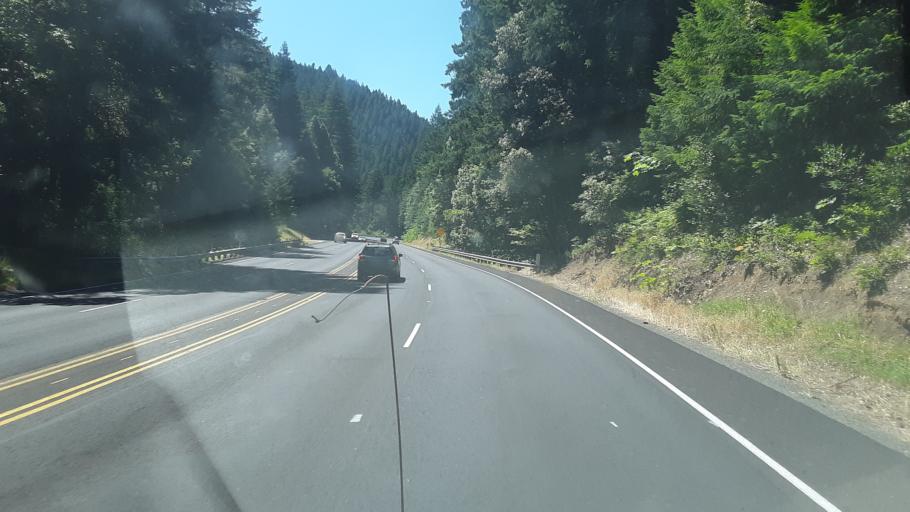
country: US
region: Oregon
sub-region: Josephine County
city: Cave Junction
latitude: 41.9116
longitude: -123.7703
